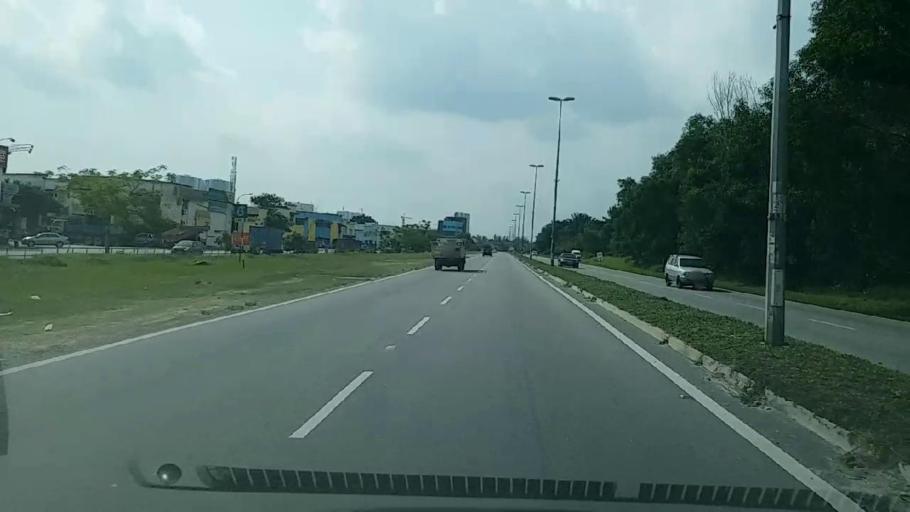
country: MY
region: Selangor
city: Subang Jaya
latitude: 2.9705
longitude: 101.6131
